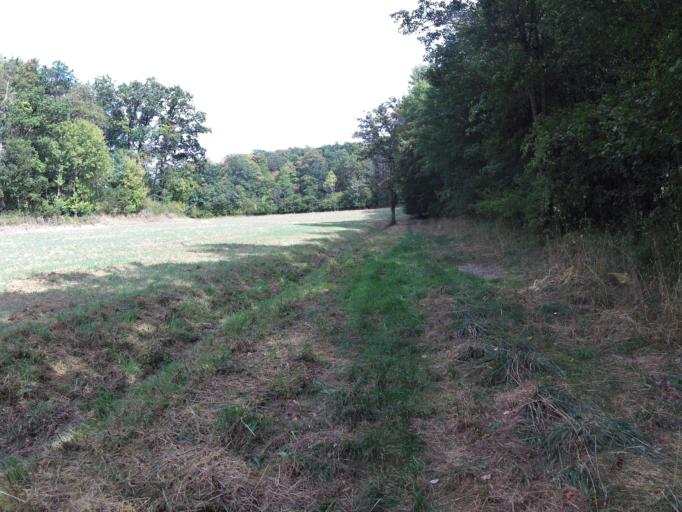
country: DE
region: Bavaria
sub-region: Regierungsbezirk Unterfranken
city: Guntersleben
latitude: 49.8611
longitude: 9.9230
